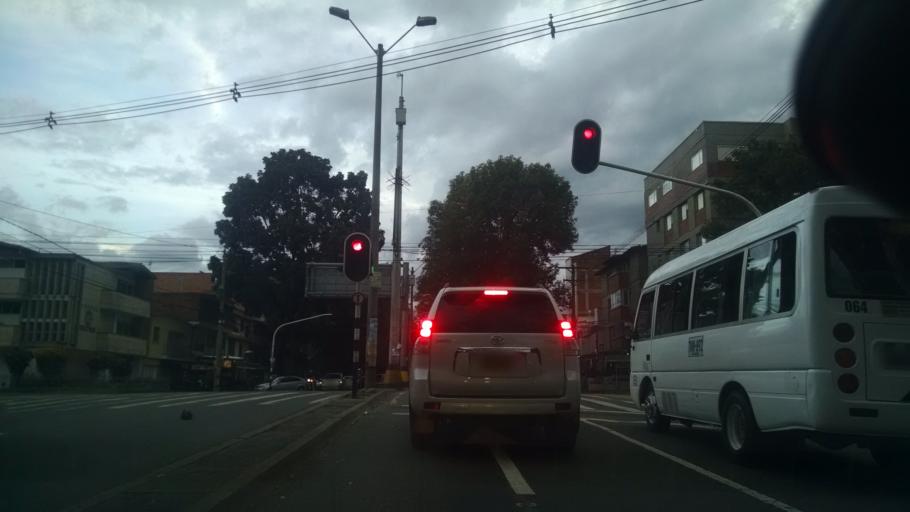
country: CO
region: Antioquia
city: Medellin
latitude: 6.2566
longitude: -75.5983
